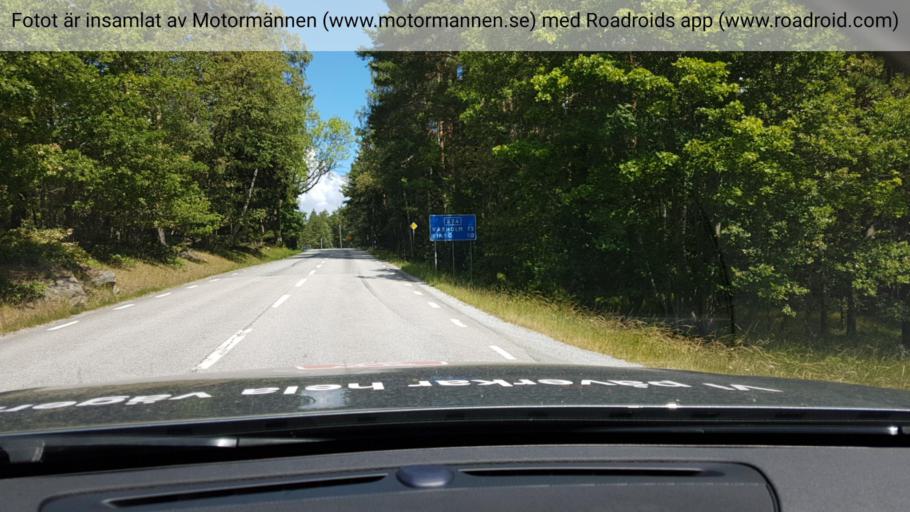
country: SE
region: Stockholm
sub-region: Varmdo Kommun
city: Hemmesta
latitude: 59.3628
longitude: 18.5180
